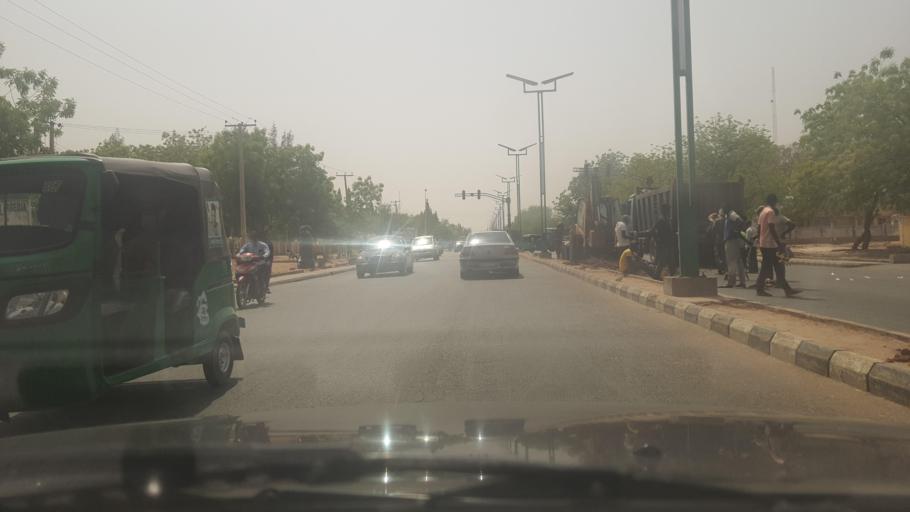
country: NG
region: Gombe
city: Gombe
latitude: 10.2838
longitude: 11.1512
